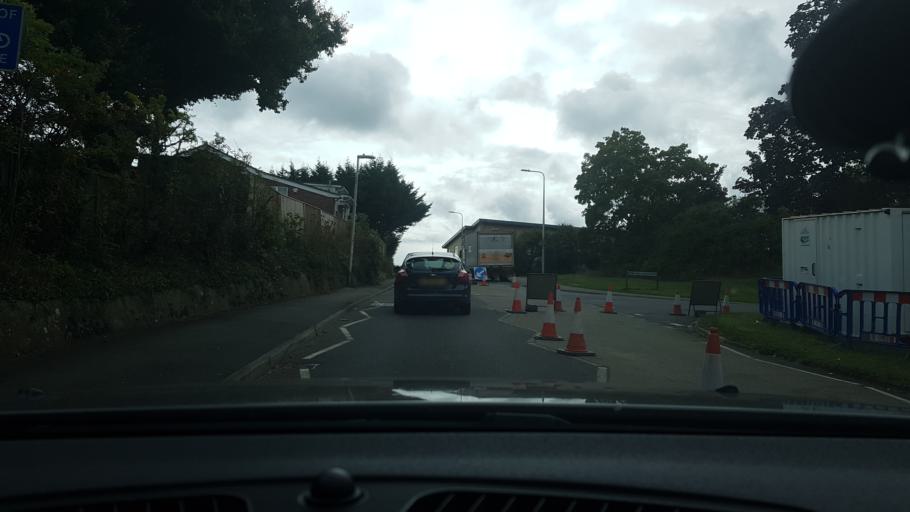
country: GB
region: England
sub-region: West Berkshire
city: Greenham
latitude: 51.3896
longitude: -1.3132
